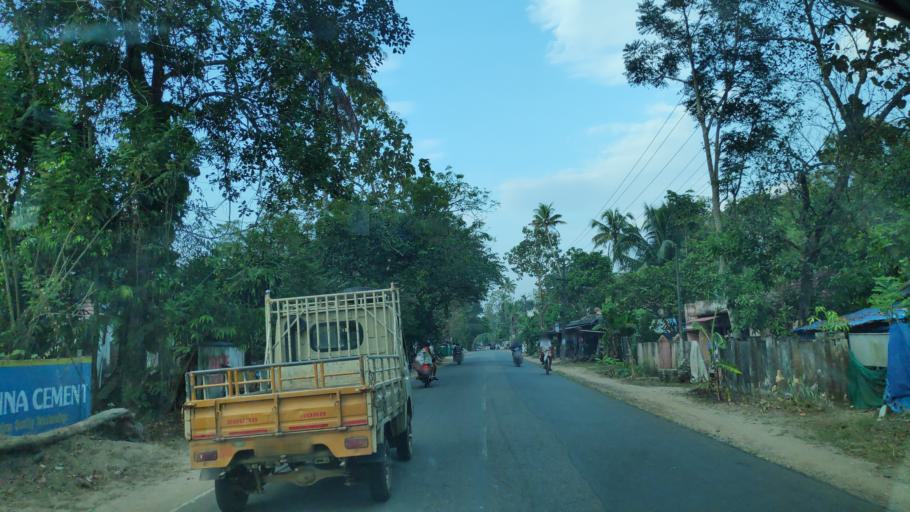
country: IN
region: Kerala
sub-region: Alappuzha
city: Shertallai
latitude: 9.6443
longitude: 76.3703
